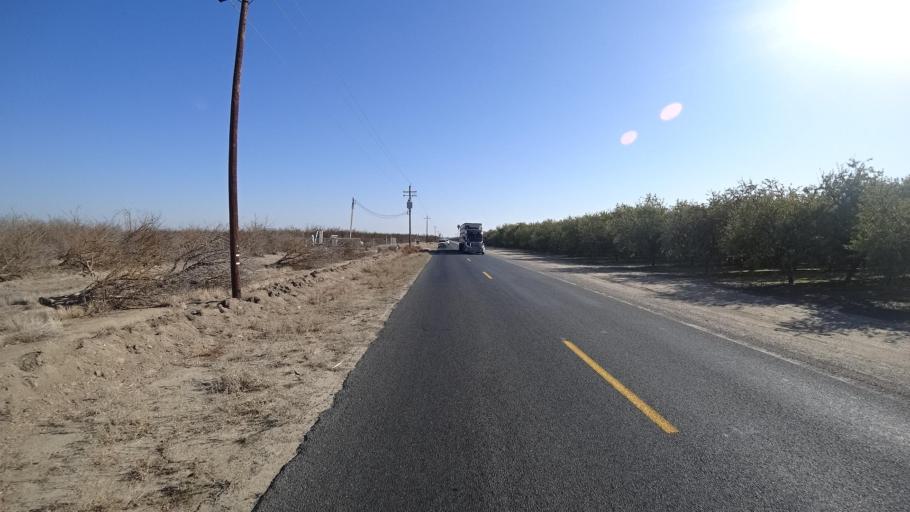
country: US
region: California
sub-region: Kern County
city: Wasco
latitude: 35.7176
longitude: -119.3800
